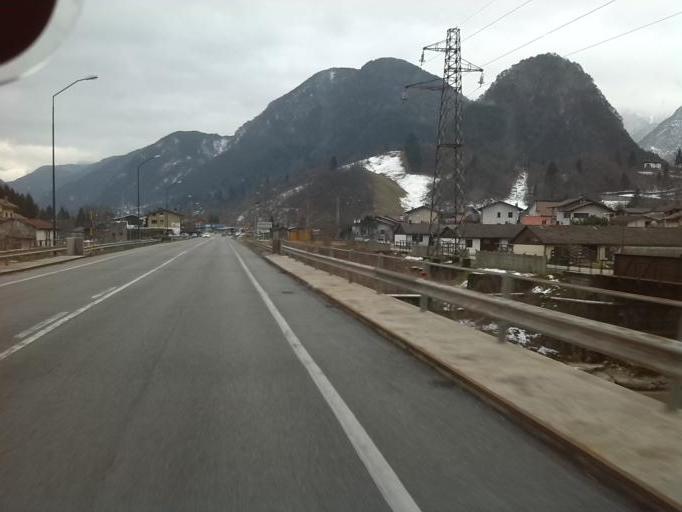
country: IT
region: Friuli Venezia Giulia
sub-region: Provincia di Udine
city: Resiutta
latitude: 46.3943
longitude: 13.2179
